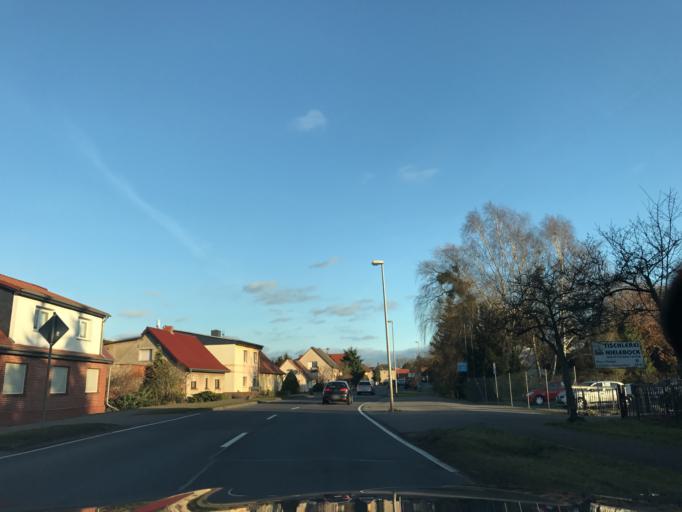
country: DE
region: Saxony-Anhalt
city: Burg bei Magdeburg
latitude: 52.2832
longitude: 11.9333
